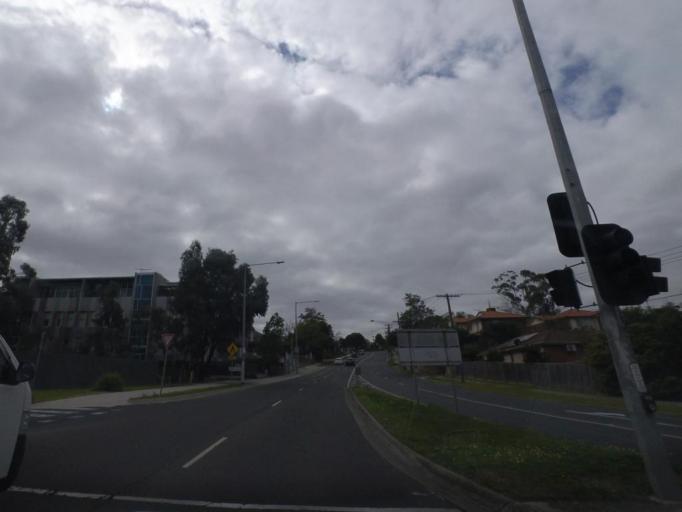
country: AU
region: Victoria
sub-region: Manningham
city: Doncaster
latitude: -37.7957
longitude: 145.1188
